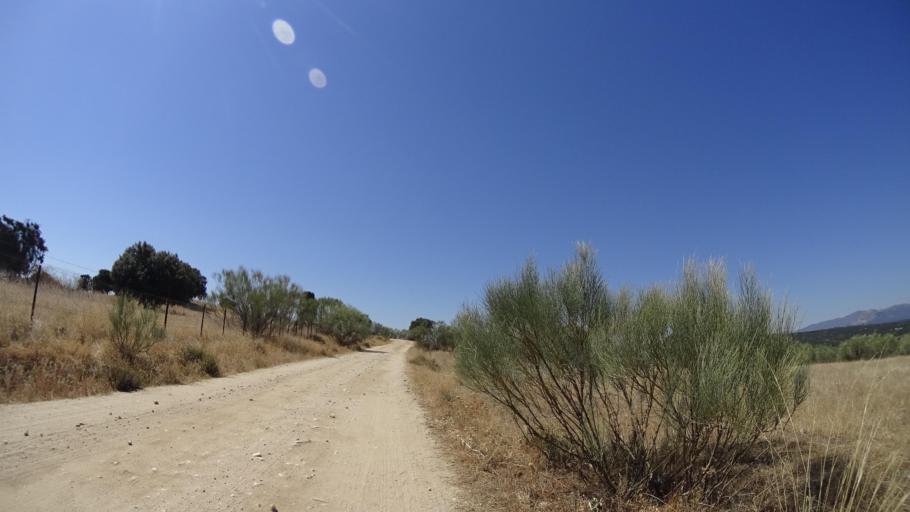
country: ES
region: Madrid
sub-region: Provincia de Madrid
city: Colmenarejo
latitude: 40.5185
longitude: -4.0130
